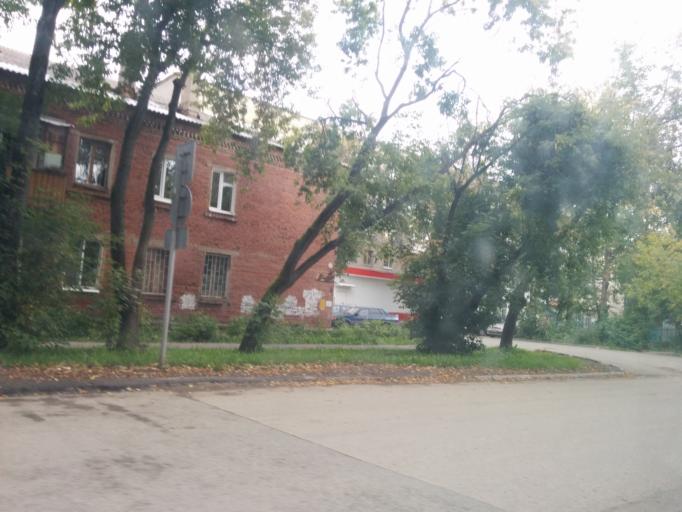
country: RU
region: Perm
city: Perm
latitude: 58.0000
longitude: 56.3006
